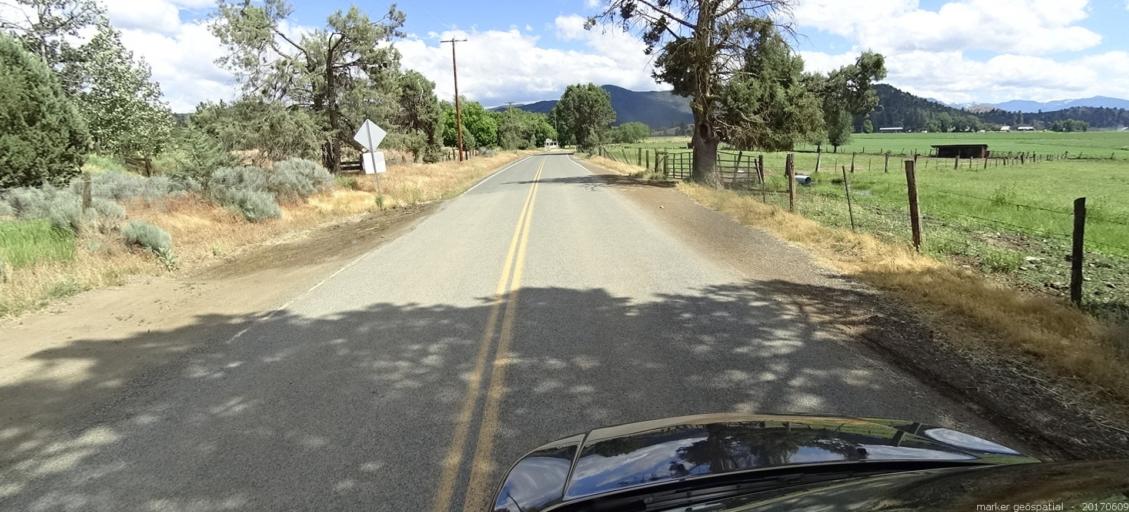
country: US
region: California
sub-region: Siskiyou County
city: Yreka
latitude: 41.5076
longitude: -122.8386
